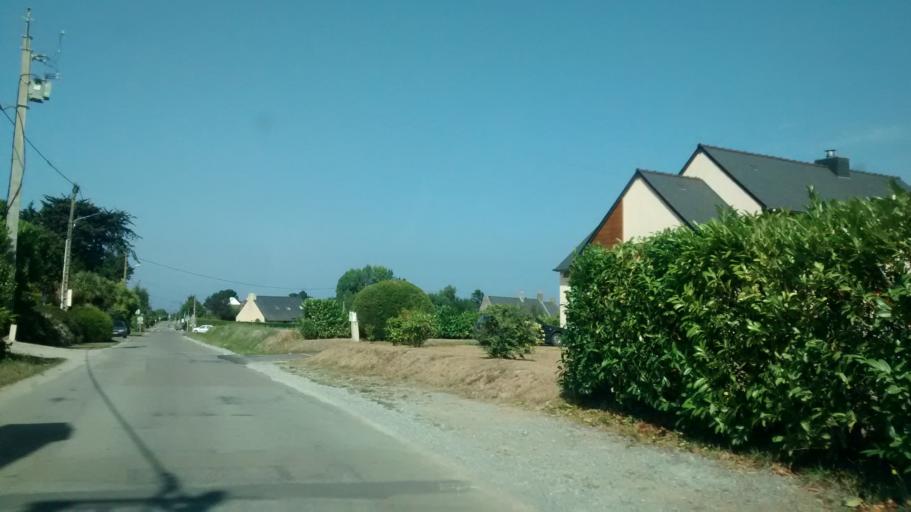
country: FR
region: Brittany
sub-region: Departement d'Ille-et-Vilaine
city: Saint-Coulomb
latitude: 48.6833
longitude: -1.8968
